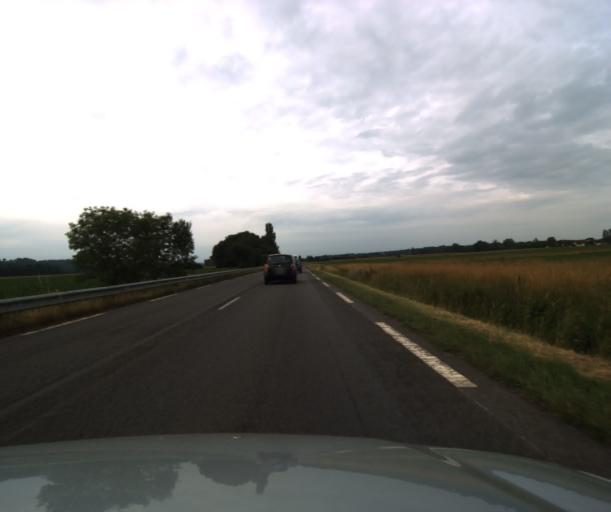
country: FR
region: Midi-Pyrenees
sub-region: Departement des Hautes-Pyrenees
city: Rabastens-de-Bigorre
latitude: 43.3511
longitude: 0.1369
